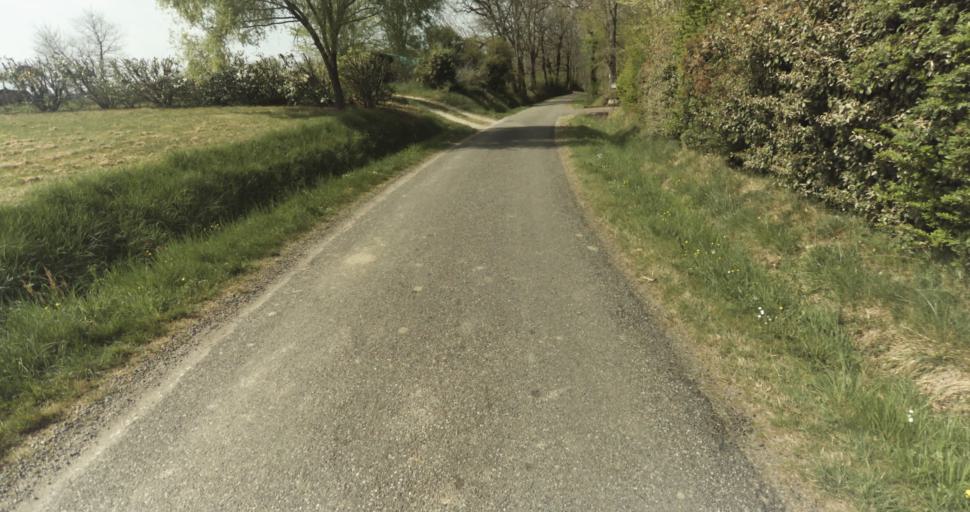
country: FR
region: Midi-Pyrenees
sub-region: Departement du Tarn-et-Garonne
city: Moissac
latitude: 44.1605
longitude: 1.1238
